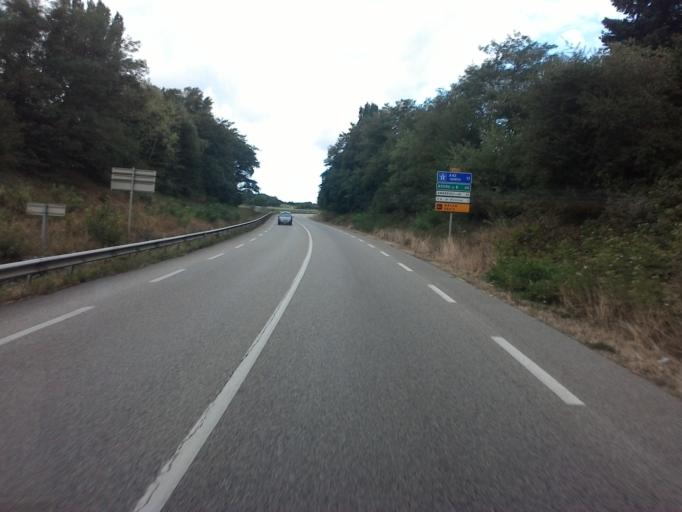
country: FR
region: Rhone-Alpes
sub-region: Departement de l'Ain
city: Lagnieu
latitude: 45.8866
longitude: 5.3446
